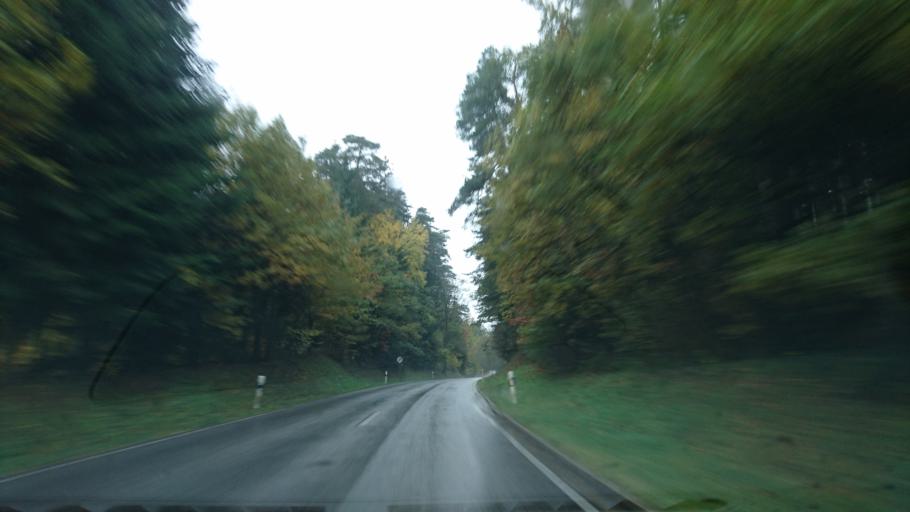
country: DE
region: Bavaria
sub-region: Upper Bavaria
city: Petershausen
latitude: 48.4165
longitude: 11.4540
